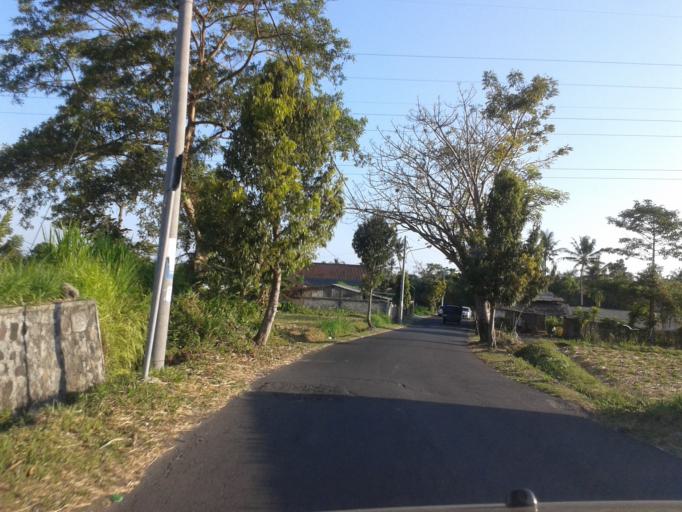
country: ID
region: Bali
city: Semarapura
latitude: -8.5624
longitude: 115.3866
